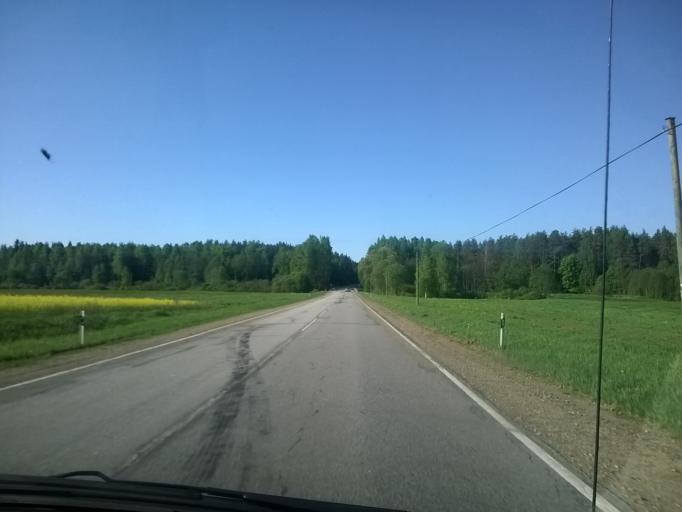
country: LV
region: Valkas Rajons
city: Valka
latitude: 57.7404
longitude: 25.9457
